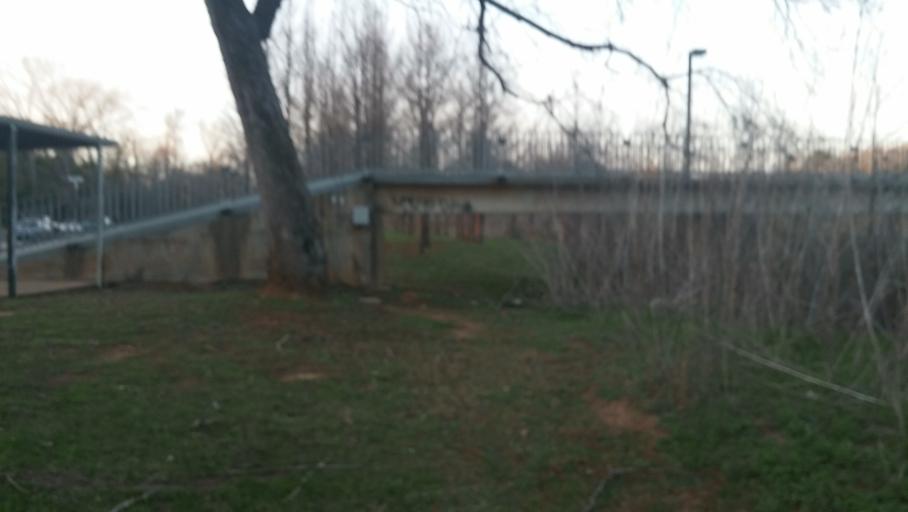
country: US
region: Texas
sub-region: Nacogdoches County
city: Nacogdoches
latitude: 31.6247
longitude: -94.6422
